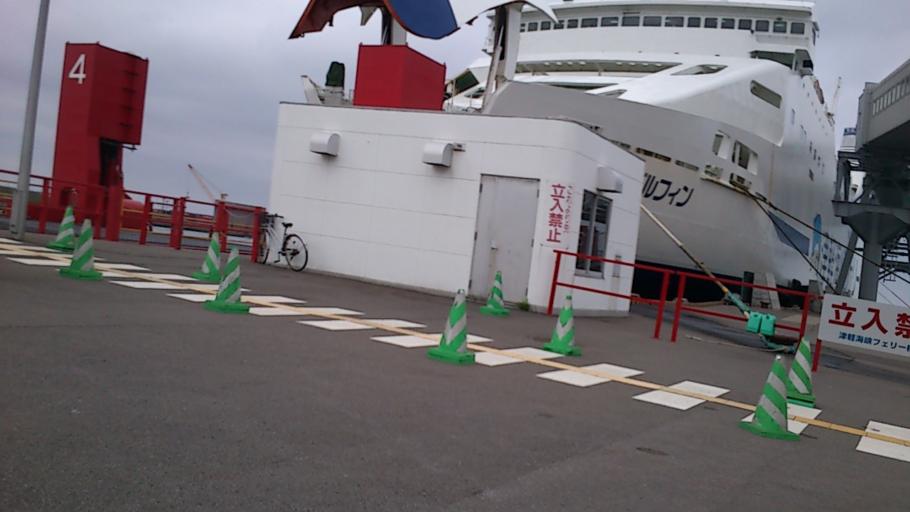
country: JP
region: Hokkaido
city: Hakodate
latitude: 41.8077
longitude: 140.7112
